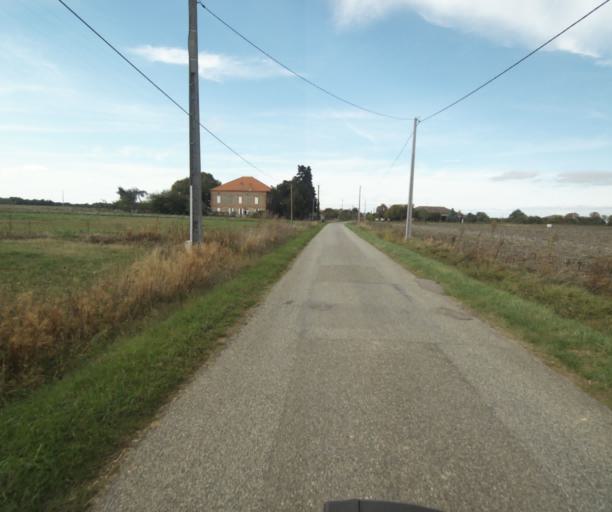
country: FR
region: Midi-Pyrenees
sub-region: Departement du Tarn-et-Garonne
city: Saint-Porquier
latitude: 43.9519
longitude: 1.1545
